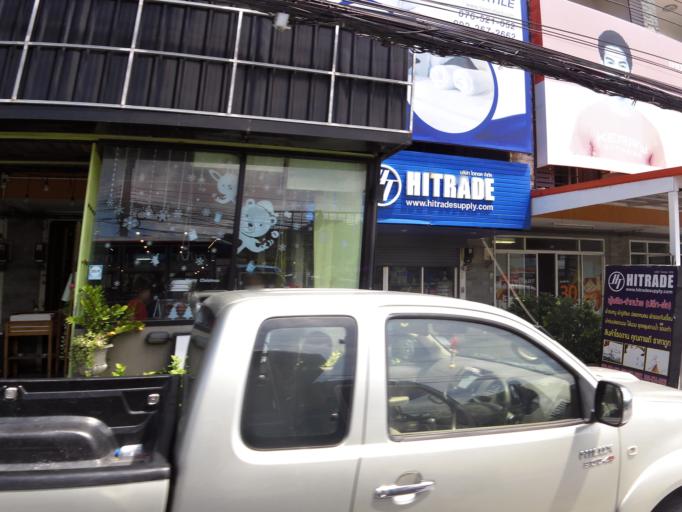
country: TH
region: Phuket
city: Ban Chalong
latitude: 7.8515
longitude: 98.3358
